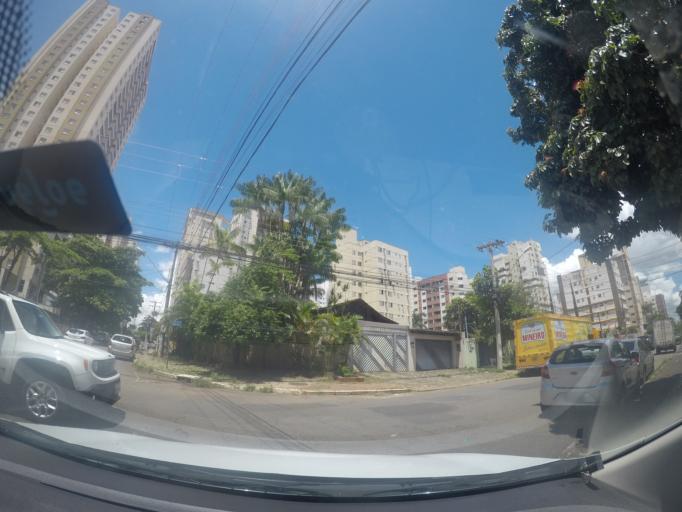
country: BR
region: Goias
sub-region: Goiania
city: Goiania
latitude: -16.7159
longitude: -49.2710
